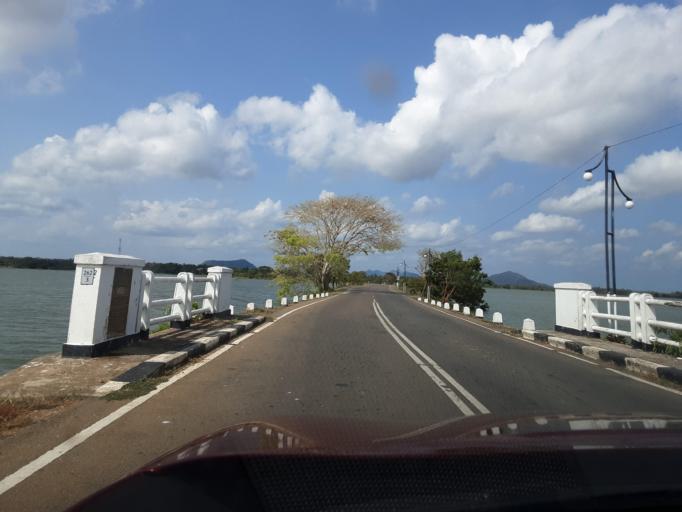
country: LK
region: Southern
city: Tangalla
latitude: 6.2867
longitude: 81.2322
